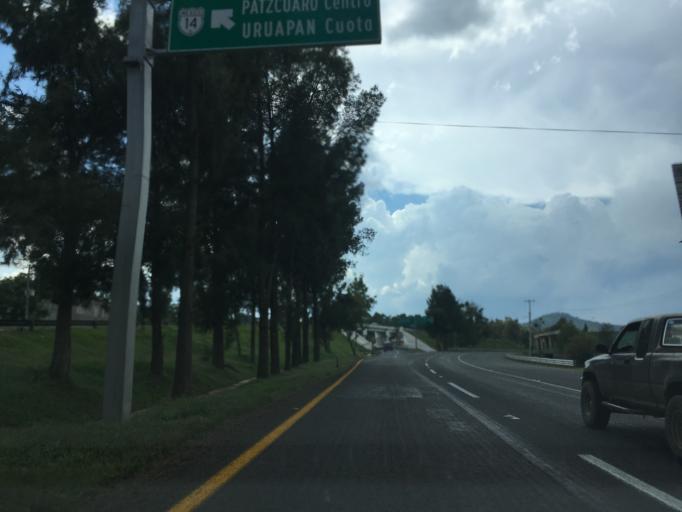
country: MX
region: Michoacan
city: Patzcuaro
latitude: 19.5310
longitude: -101.5591
